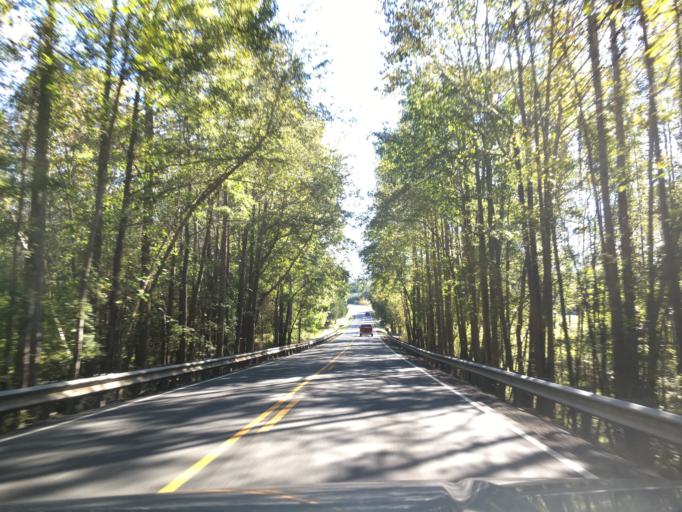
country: US
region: Virginia
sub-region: Goochland County
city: Goochland
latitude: 37.6968
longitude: -77.8776
